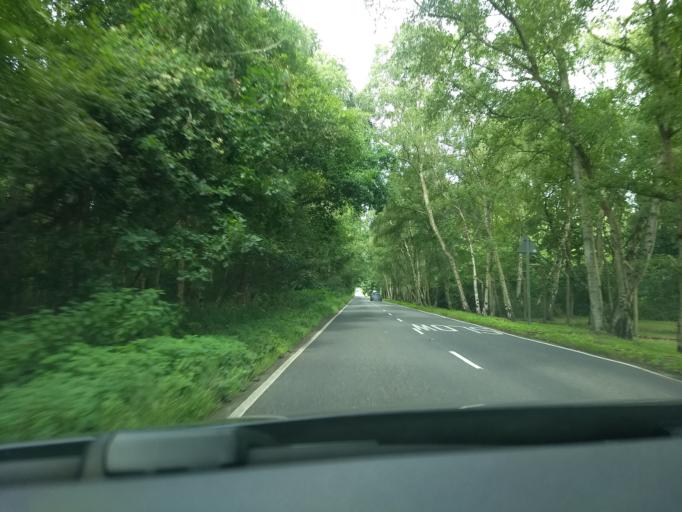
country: GB
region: England
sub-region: Suffolk
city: Woodbridge
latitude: 52.0810
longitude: 1.3828
